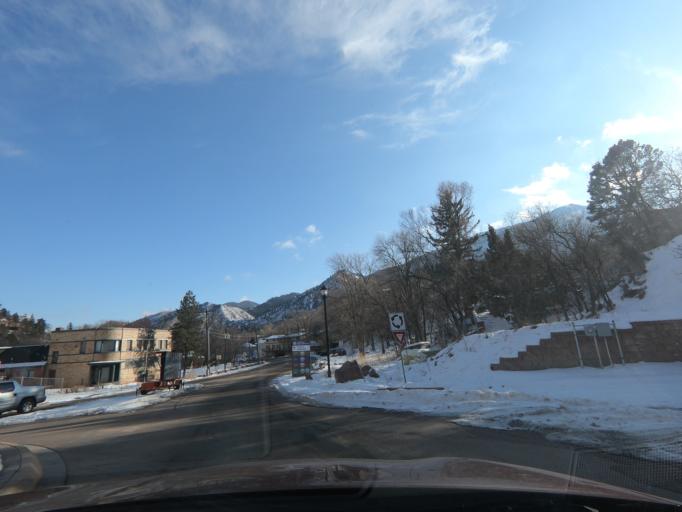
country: US
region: Colorado
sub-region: El Paso County
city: Manitou Springs
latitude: 38.8638
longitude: -104.9227
